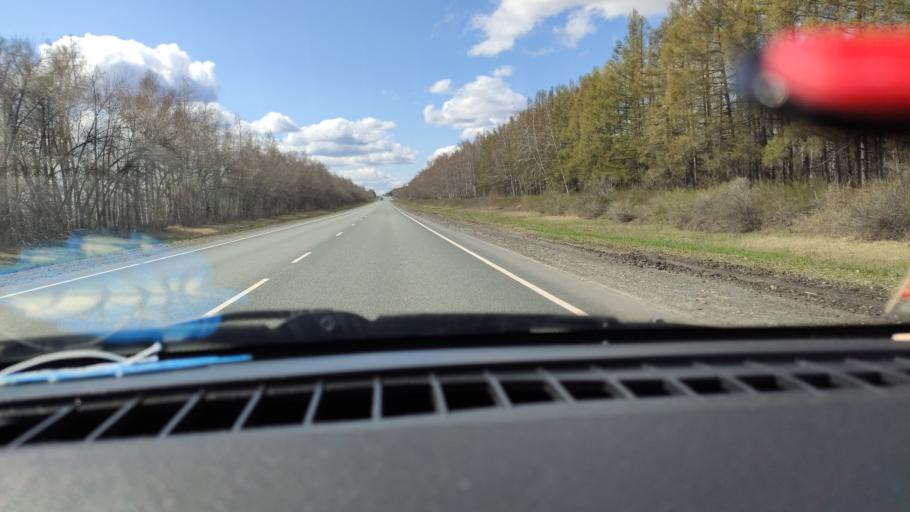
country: RU
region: Saratov
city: Khvalynsk
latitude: 52.5684
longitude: 48.0989
